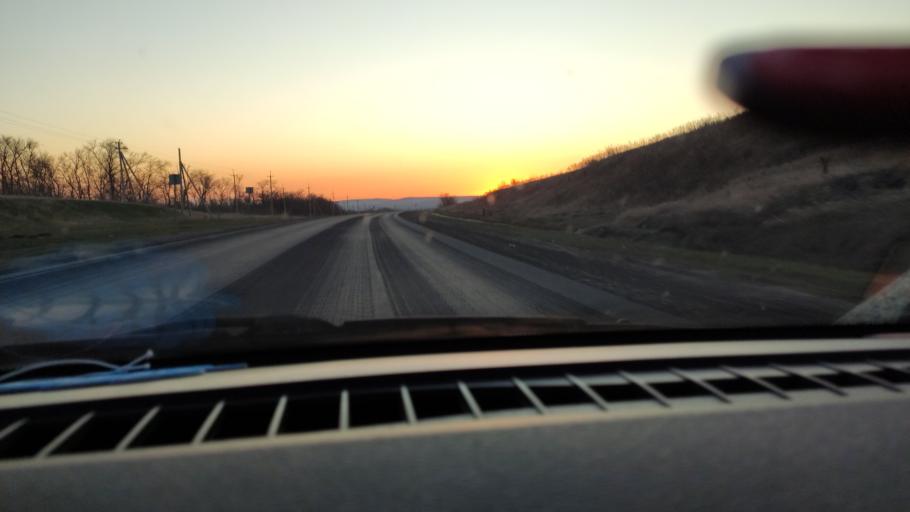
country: RU
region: Saratov
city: Shumeyka
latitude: 51.7855
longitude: 46.1361
